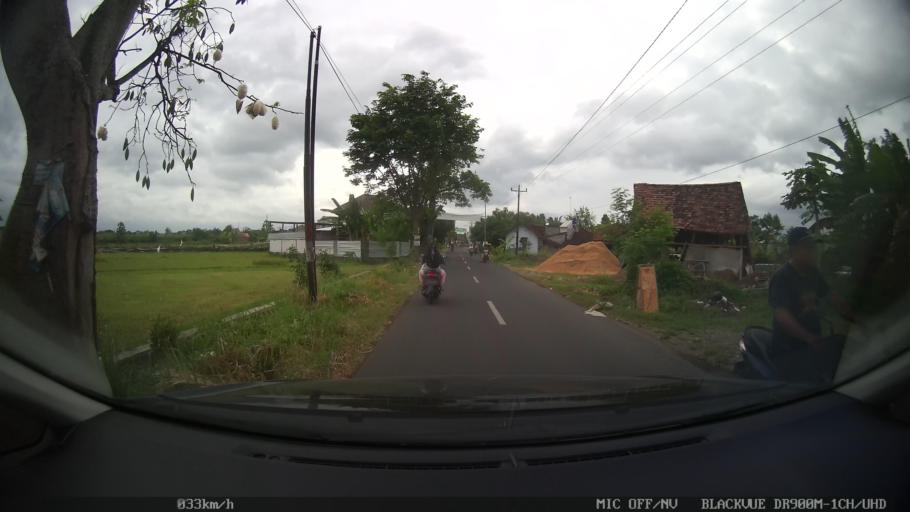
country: ID
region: Daerah Istimewa Yogyakarta
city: Sewon
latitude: -7.8378
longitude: 110.4133
